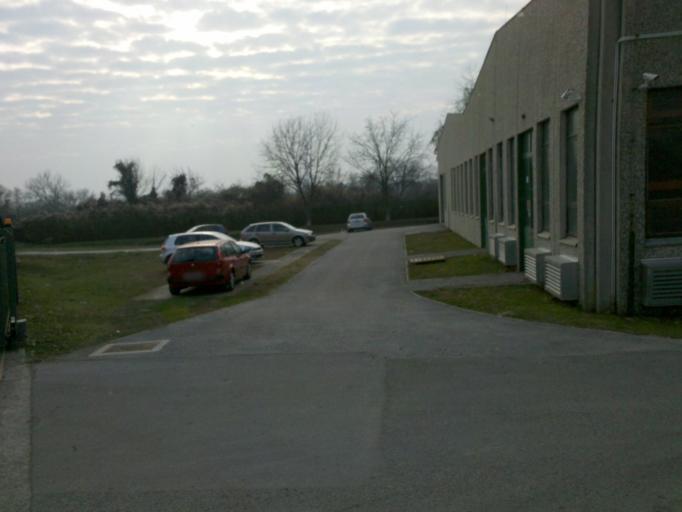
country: HR
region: Grad Zagreb
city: Novi Zagreb
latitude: 45.7819
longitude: 16.0299
